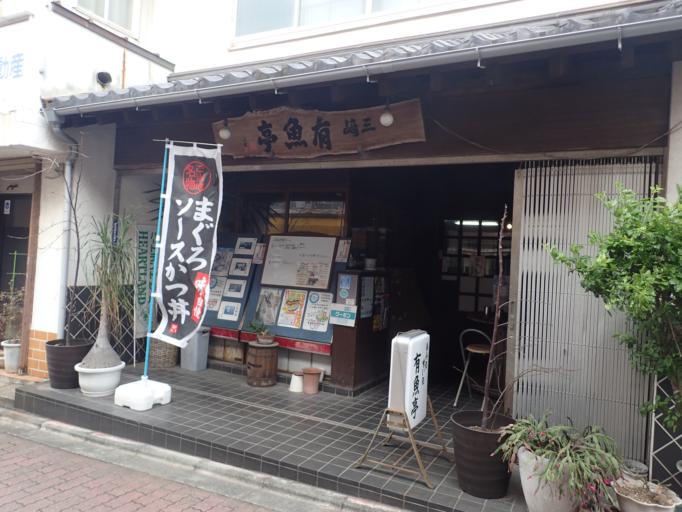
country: JP
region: Kanagawa
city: Miura
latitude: 35.1406
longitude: 139.6190
